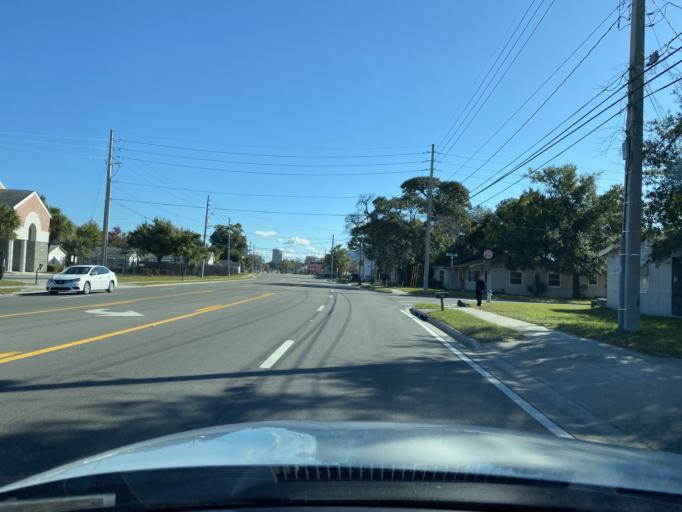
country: US
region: Florida
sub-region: Orange County
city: Orlando
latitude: 28.5439
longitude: -81.4020
